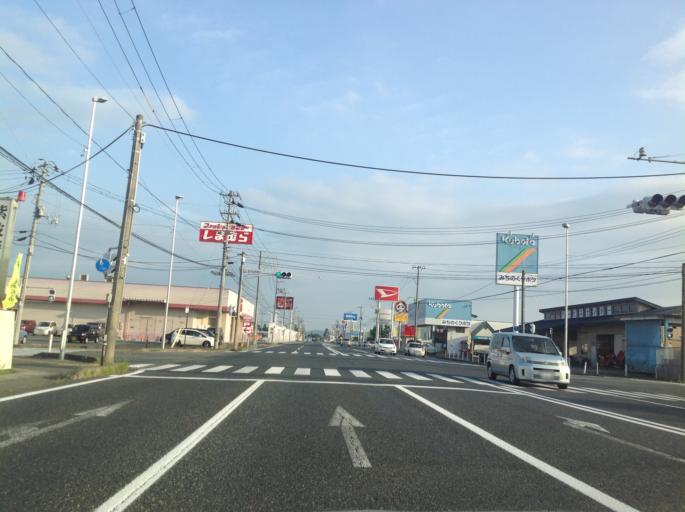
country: JP
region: Iwate
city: Morioka-shi
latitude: 39.5481
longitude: 141.1680
